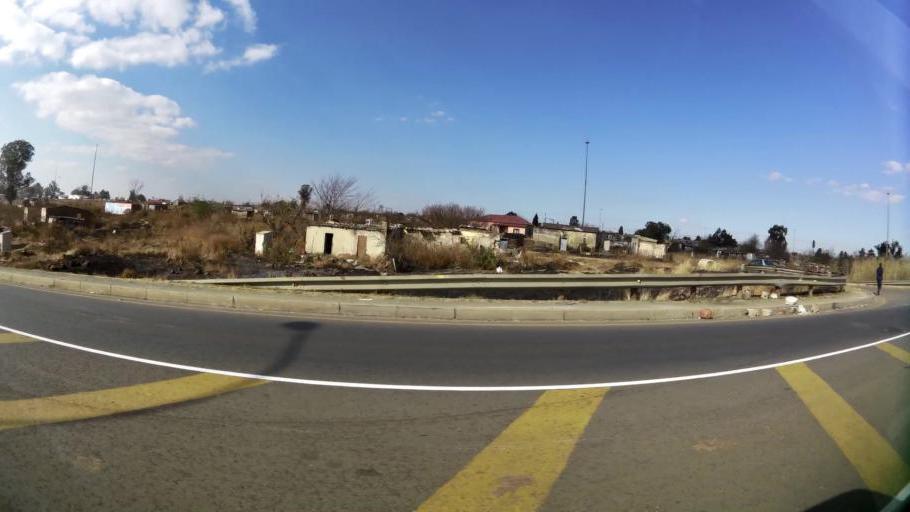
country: ZA
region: Gauteng
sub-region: City of Johannesburg Metropolitan Municipality
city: Soweto
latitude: -26.2656
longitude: 27.8895
